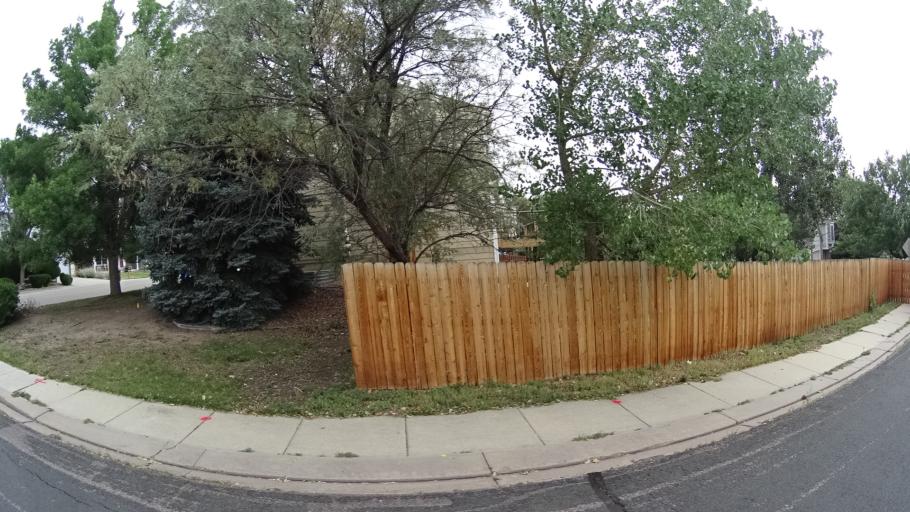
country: US
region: Colorado
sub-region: El Paso County
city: Air Force Academy
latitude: 38.9226
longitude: -104.8404
